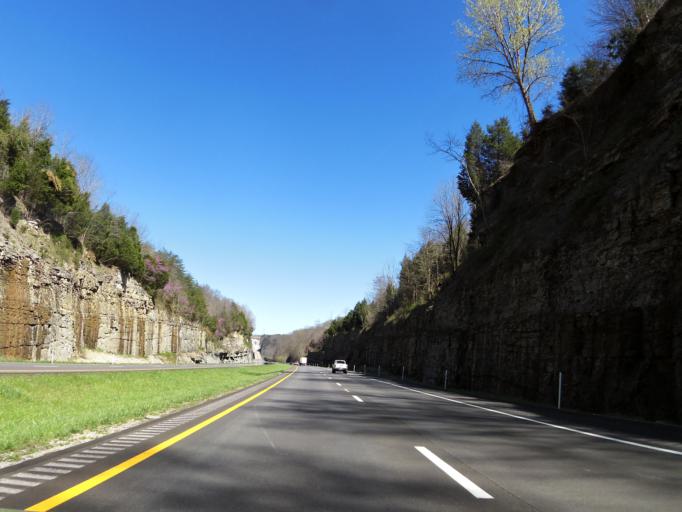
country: US
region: Kentucky
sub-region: Pulaski County
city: Somerset
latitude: 37.0956
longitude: -84.7097
